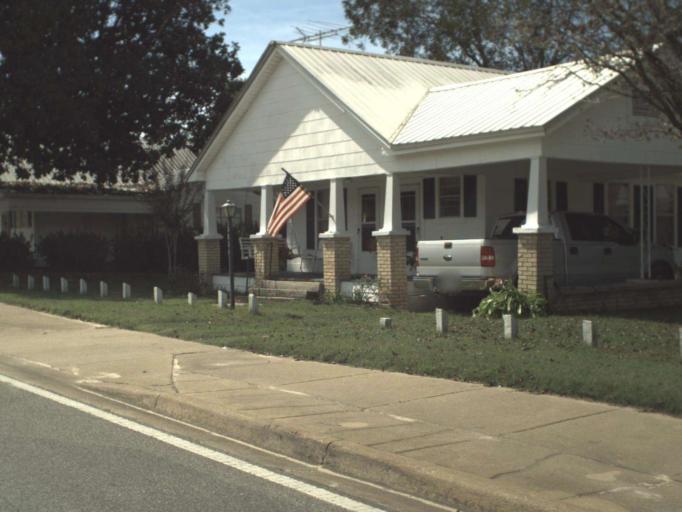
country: US
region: Florida
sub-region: Washington County
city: Chipley
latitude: 30.6319
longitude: -85.5888
